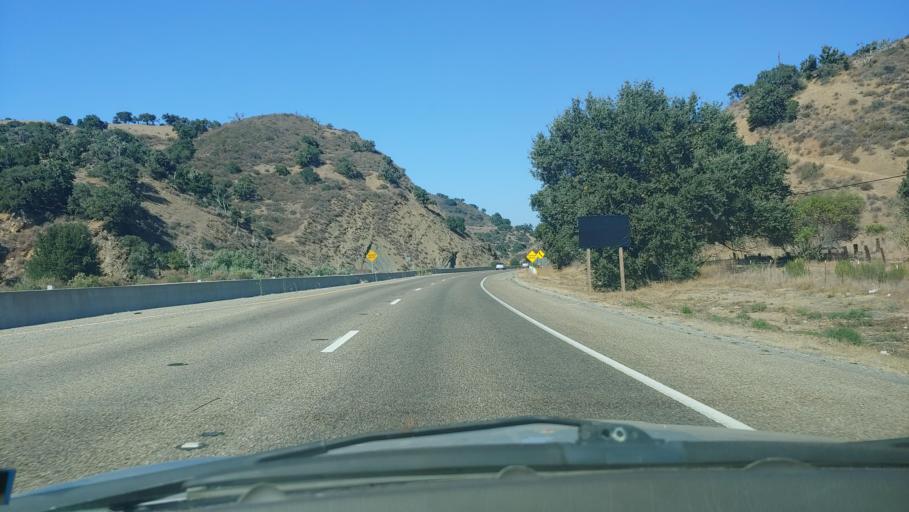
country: US
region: California
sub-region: Santa Barbara County
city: Buellton
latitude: 34.5762
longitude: -120.1938
